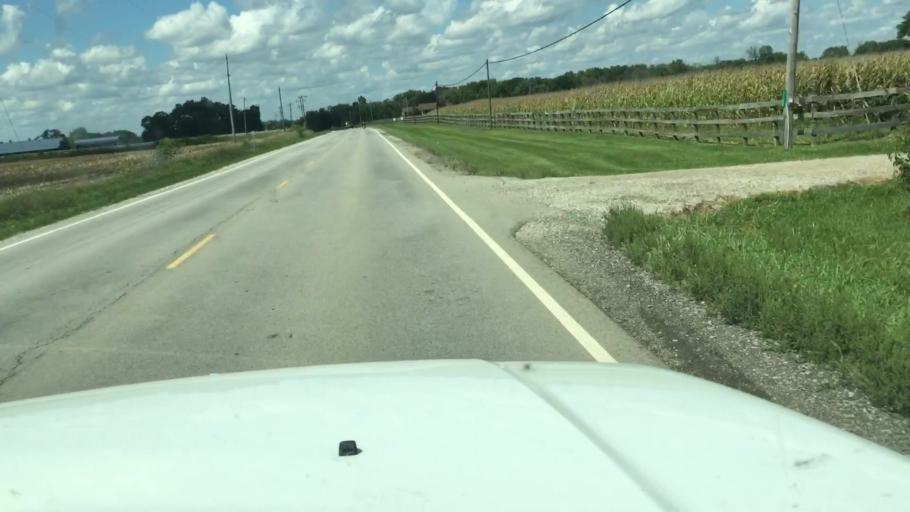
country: US
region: Ohio
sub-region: Madison County
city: Mount Sterling
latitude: 39.7490
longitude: -83.2883
